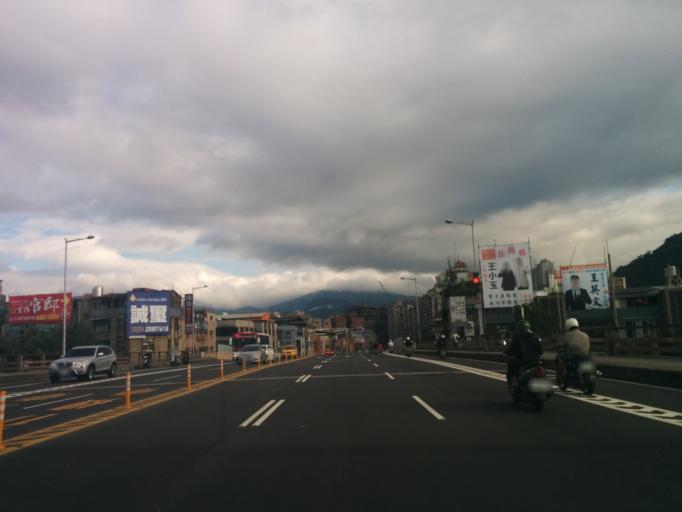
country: TW
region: Taipei
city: Taipei
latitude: 25.0781
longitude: 121.5212
